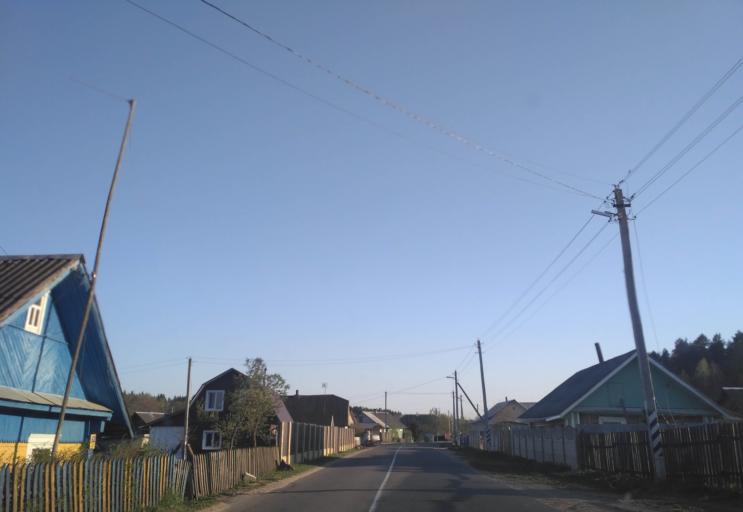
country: BY
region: Minsk
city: Radashkovichy
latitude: 54.1507
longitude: 27.2171
